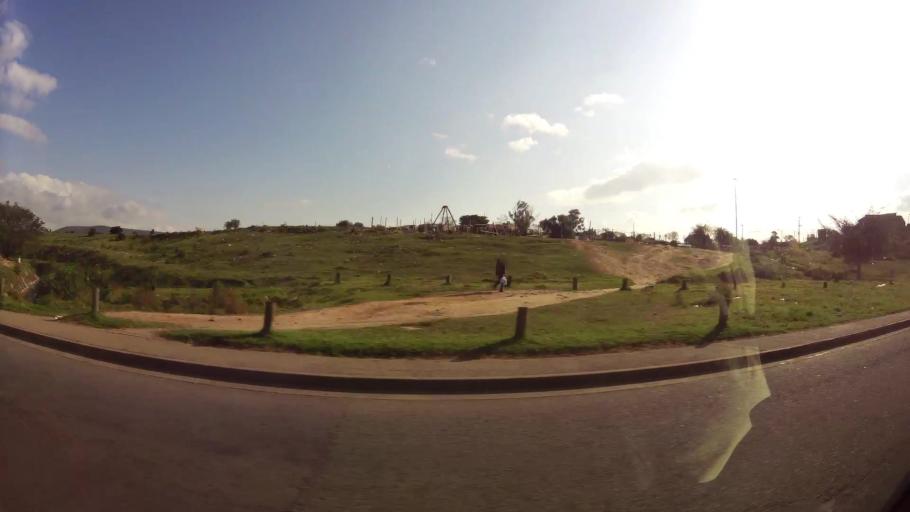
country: ZA
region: Eastern Cape
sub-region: Nelson Mandela Bay Metropolitan Municipality
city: Uitenhage
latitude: -33.7574
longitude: 25.3880
